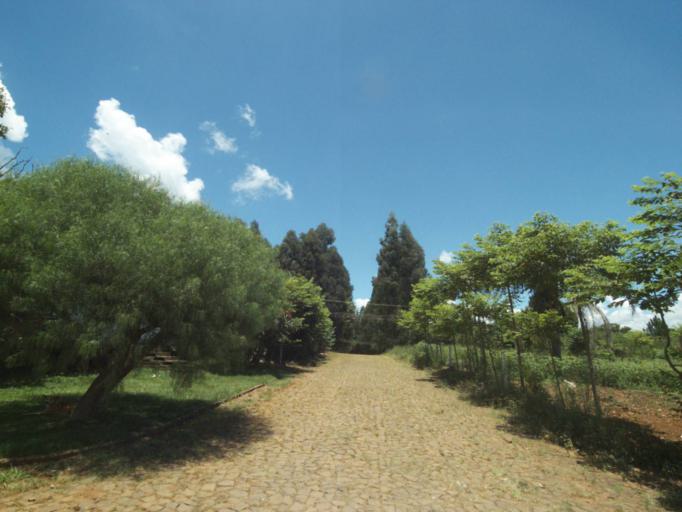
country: BR
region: Parana
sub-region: Pinhao
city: Pinhao
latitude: -25.7883
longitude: -52.0873
